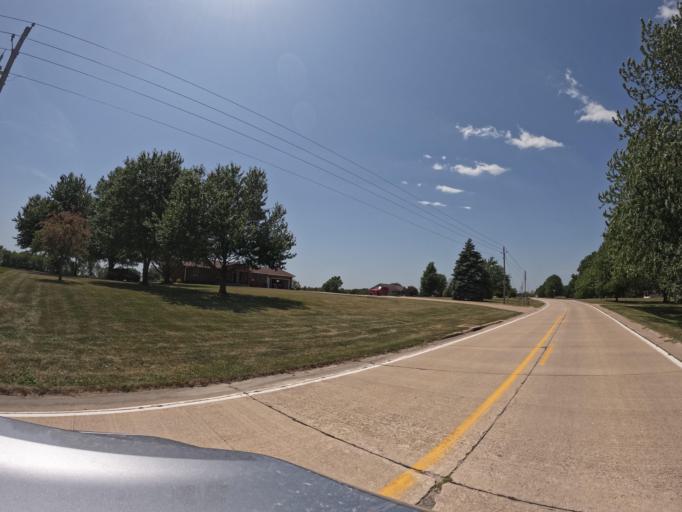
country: US
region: Iowa
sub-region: Henry County
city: Mount Pleasant
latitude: 40.9770
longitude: -91.5862
